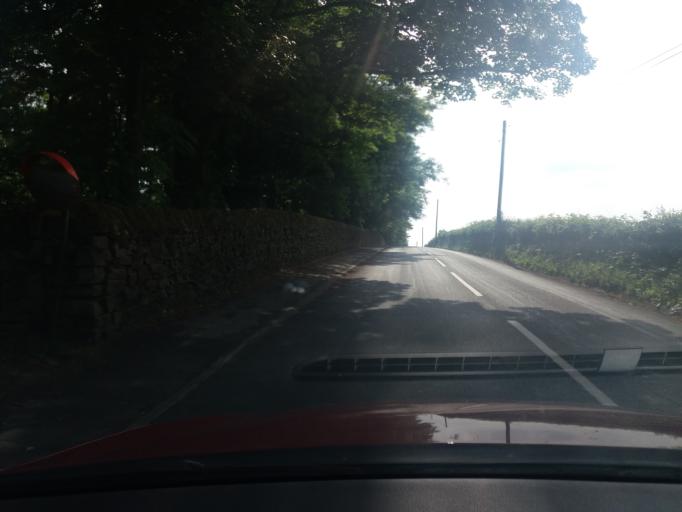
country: GB
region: England
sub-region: Borough of Wigan
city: Haigh
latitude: 53.6222
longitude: -2.5786
